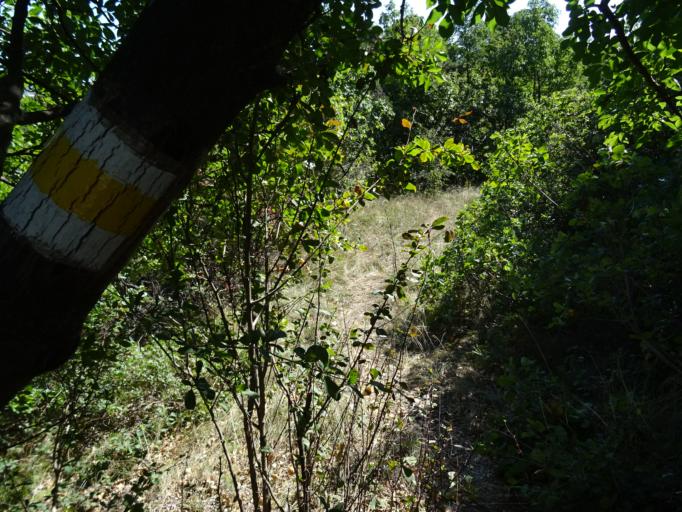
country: HU
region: Veszprem
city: Petfuerdo
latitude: 47.1665
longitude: 18.1138
